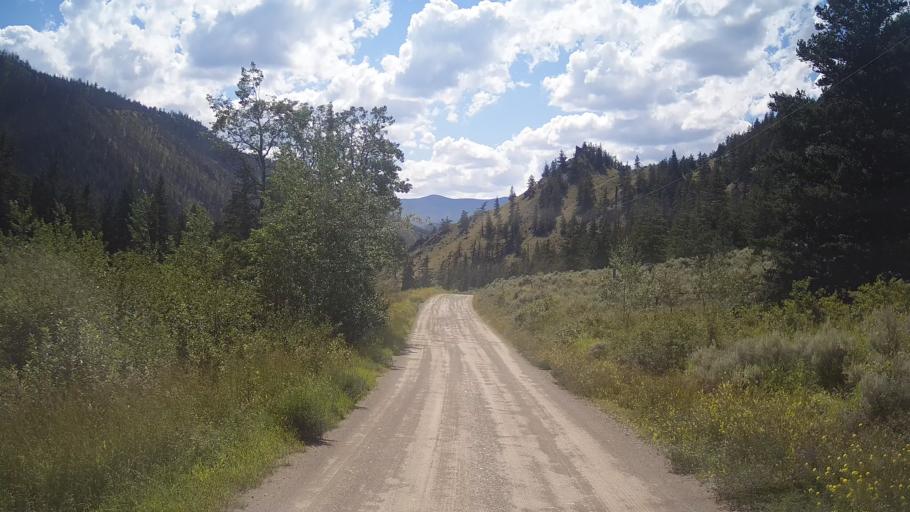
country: CA
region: British Columbia
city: Lillooet
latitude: 51.2320
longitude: -122.0553
